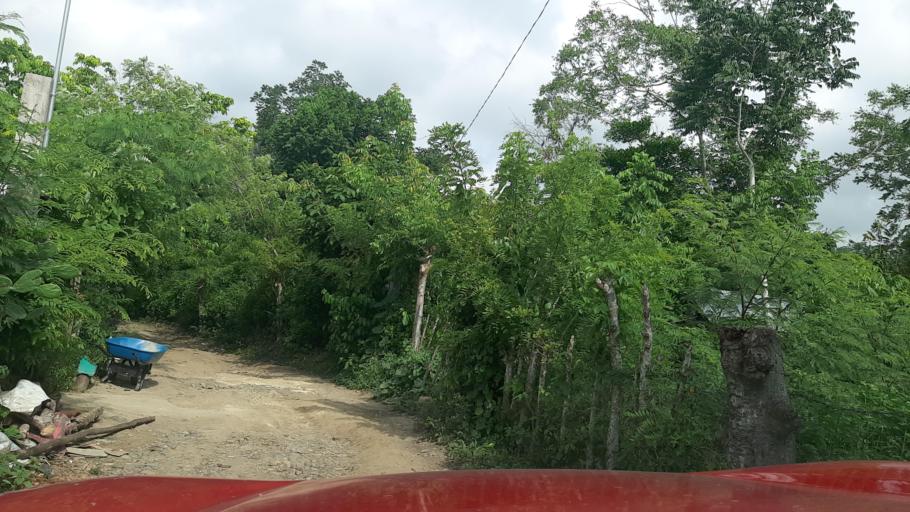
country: MX
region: Veracruz
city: Cazones de Herrera
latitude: 20.6734
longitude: -97.3250
